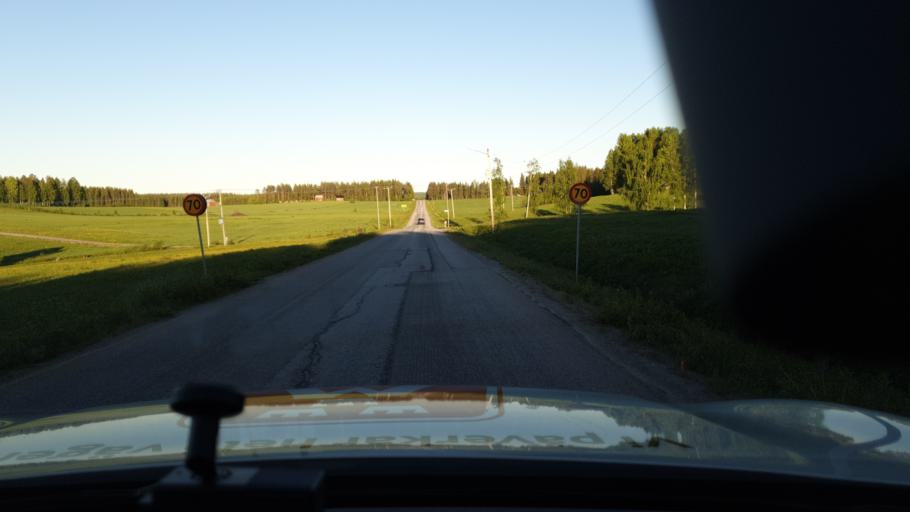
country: SE
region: Vaesterbotten
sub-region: Umea Kommun
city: Roback
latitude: 64.0256
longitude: 20.0885
